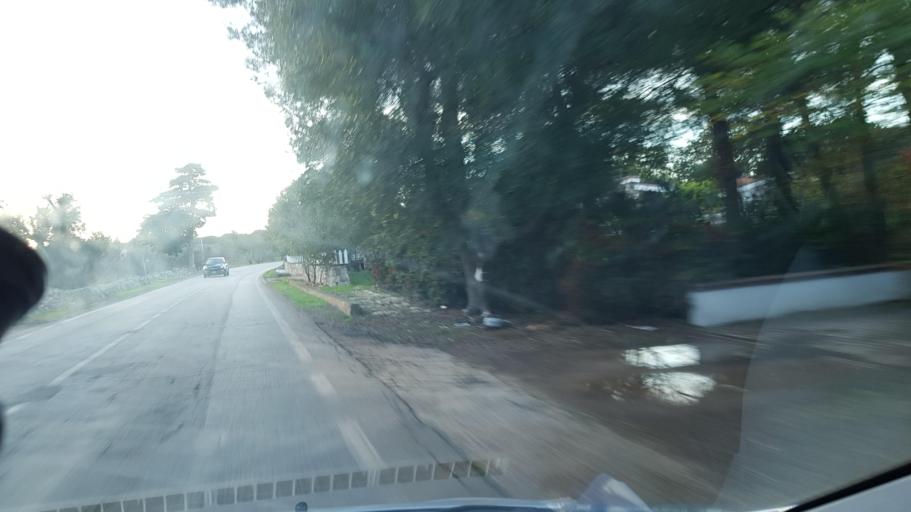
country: IT
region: Apulia
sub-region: Provincia di Brindisi
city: San Michele Salentino
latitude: 40.6409
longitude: 17.5837
